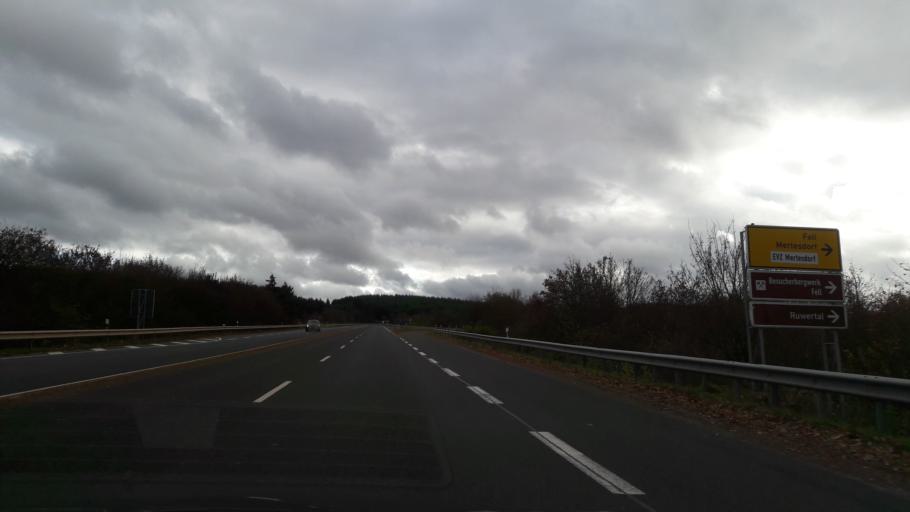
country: DE
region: Rheinland-Pfalz
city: Mertesdorf
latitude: 49.7747
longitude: 6.7513
